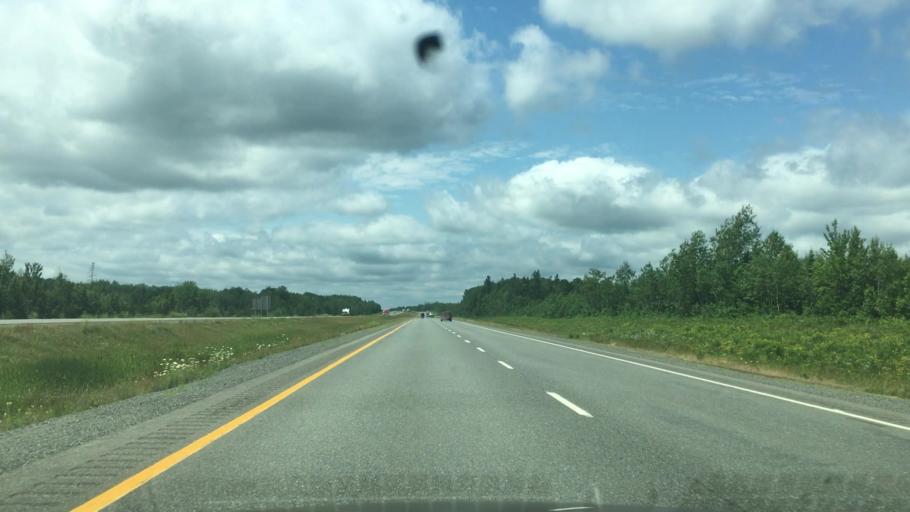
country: CA
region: Nova Scotia
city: Oxford
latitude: 45.7148
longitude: -63.9316
